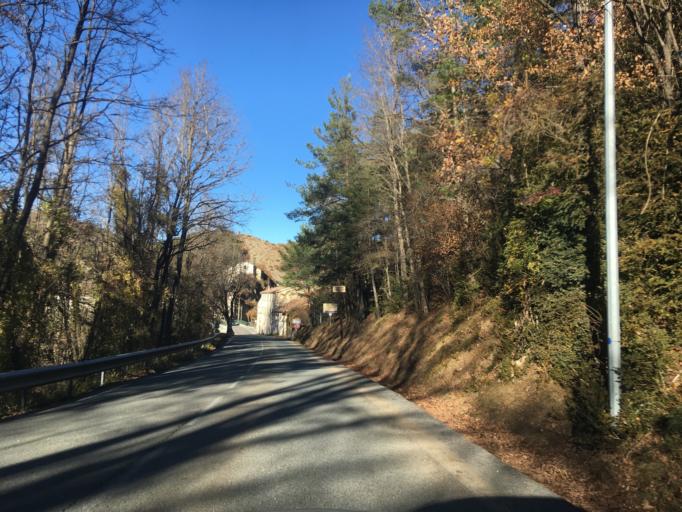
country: FR
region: Provence-Alpes-Cote d'Azur
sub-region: Departement des Alpes-de-Haute-Provence
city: Castellane
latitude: 43.7403
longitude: 6.4990
